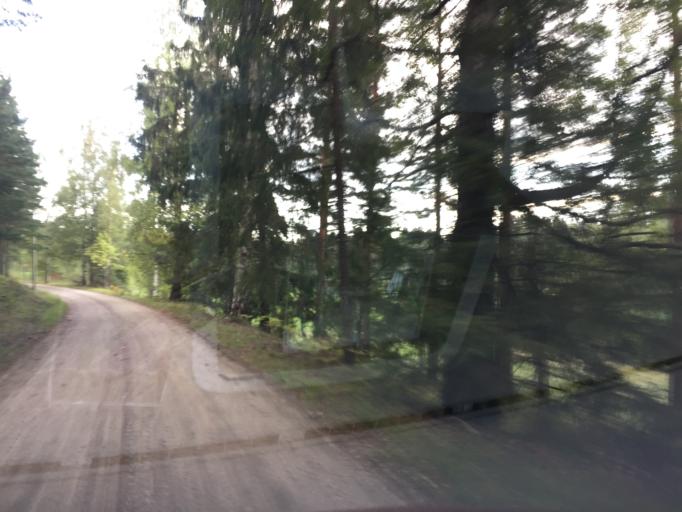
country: SE
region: Soedermanland
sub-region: Vingakers Kommun
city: Vingaker
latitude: 58.9903
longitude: 15.7327
